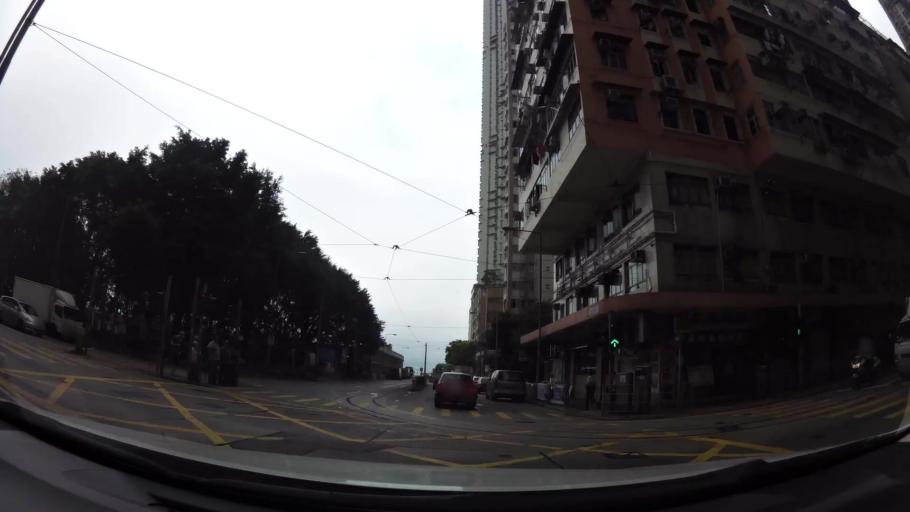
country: HK
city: Hong Kong
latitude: 22.2822
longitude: 114.1261
